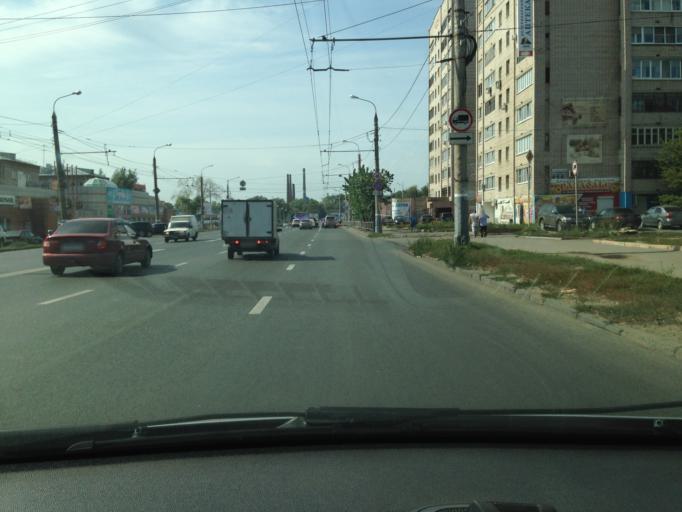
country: RU
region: Udmurtiya
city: Izhevsk
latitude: 56.8375
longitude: 53.2086
